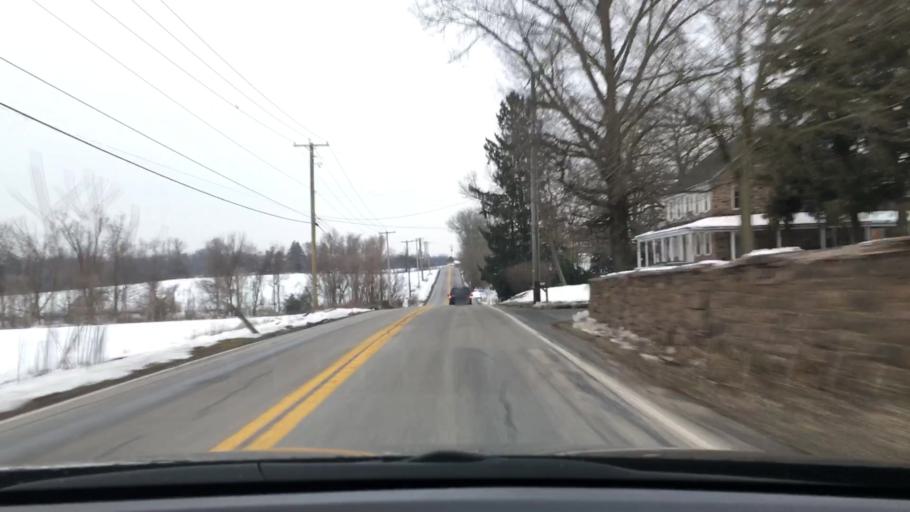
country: US
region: Pennsylvania
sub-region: York County
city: Emigsville
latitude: 40.0426
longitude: -76.7764
